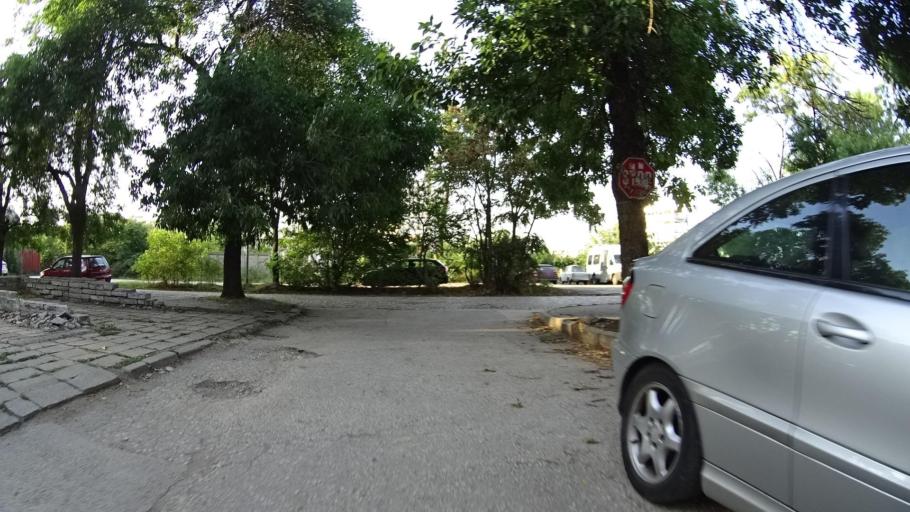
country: BG
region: Plovdiv
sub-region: Obshtina Plovdiv
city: Plovdiv
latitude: 42.1344
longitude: 24.7495
